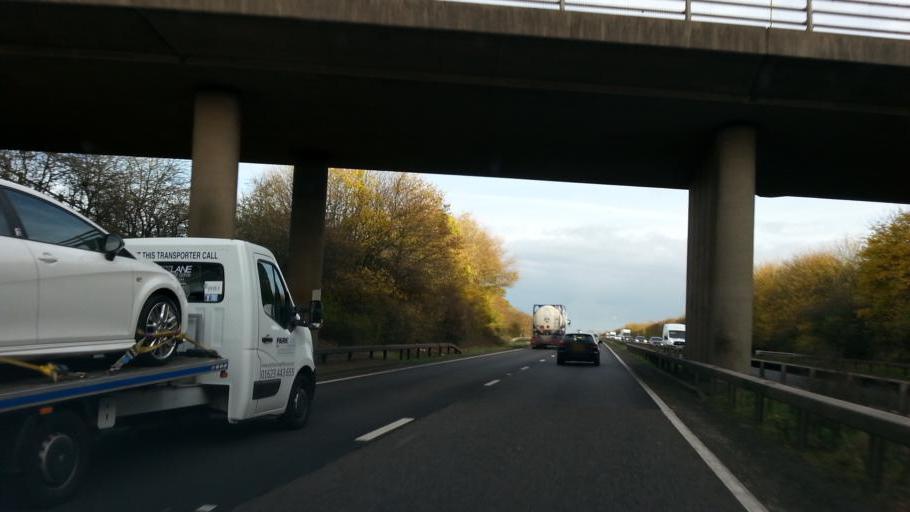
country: GB
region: England
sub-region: Leicestershire
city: Castle Donington
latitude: 52.7987
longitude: -1.3705
